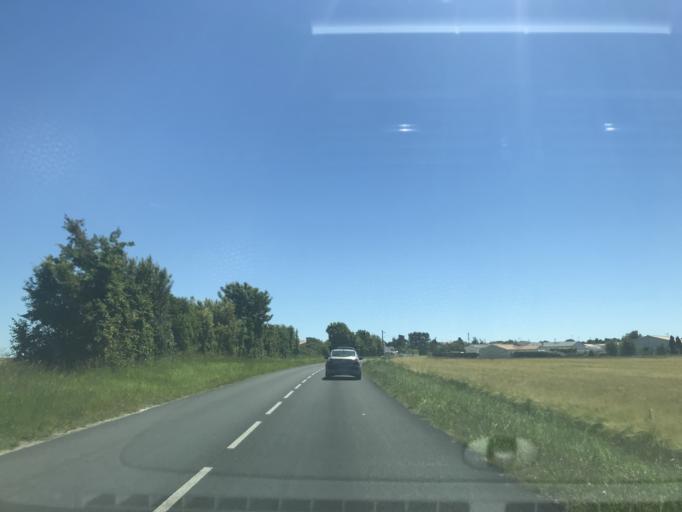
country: FR
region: Poitou-Charentes
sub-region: Departement de la Charente-Maritime
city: Meschers-sur-Gironde
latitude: 45.5799
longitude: -0.9592
